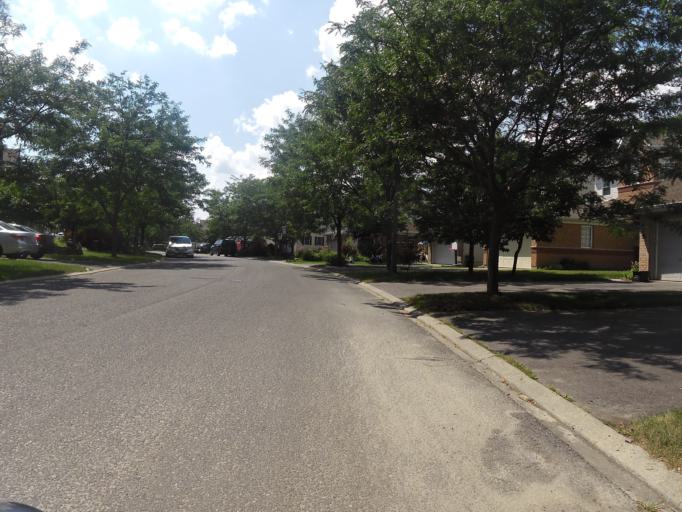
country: CA
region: Ontario
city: Bells Corners
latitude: 45.3152
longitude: -75.9288
